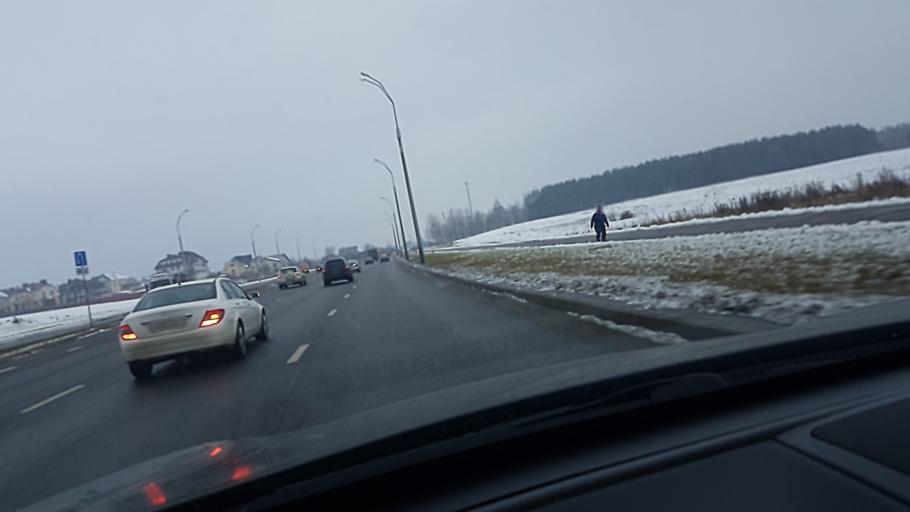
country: BY
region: Minsk
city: Minsk
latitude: 53.9490
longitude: 27.5363
